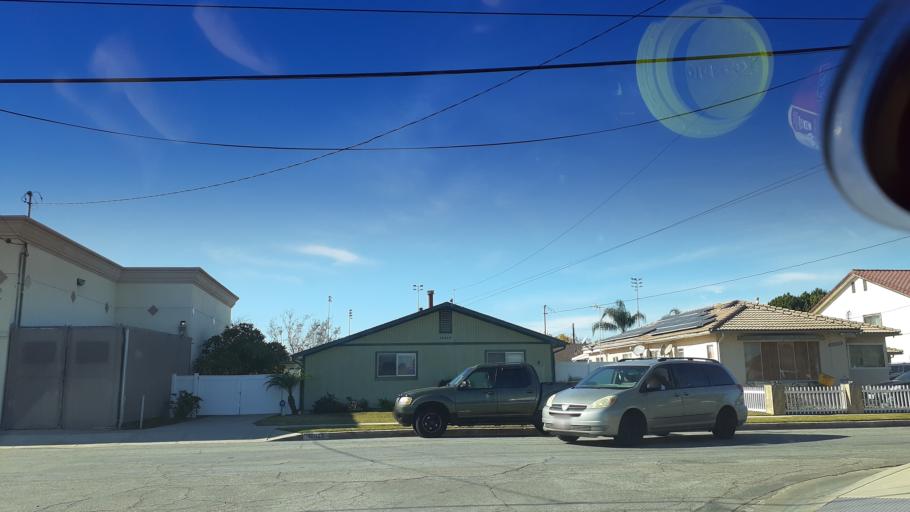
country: US
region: California
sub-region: Los Angeles County
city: Artesia
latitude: 33.8590
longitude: -118.0755
